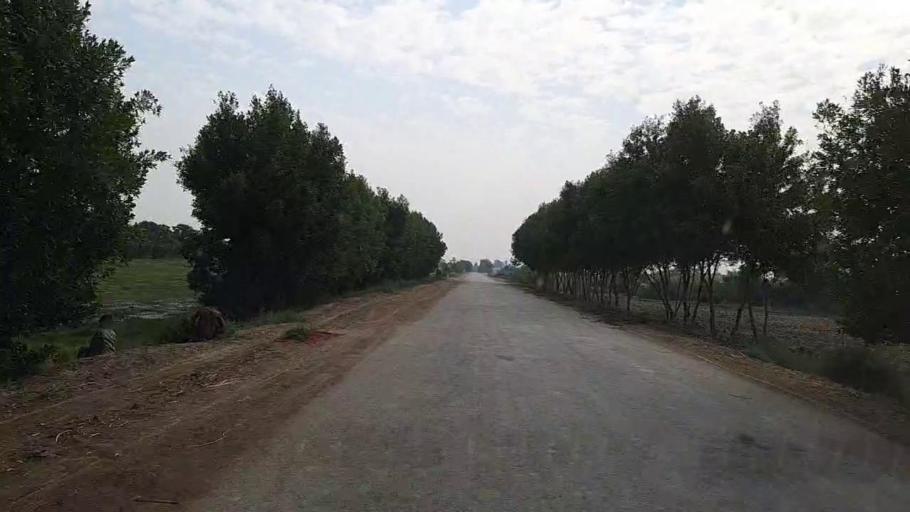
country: PK
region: Sindh
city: Mirwah Gorchani
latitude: 25.3756
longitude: 69.0818
